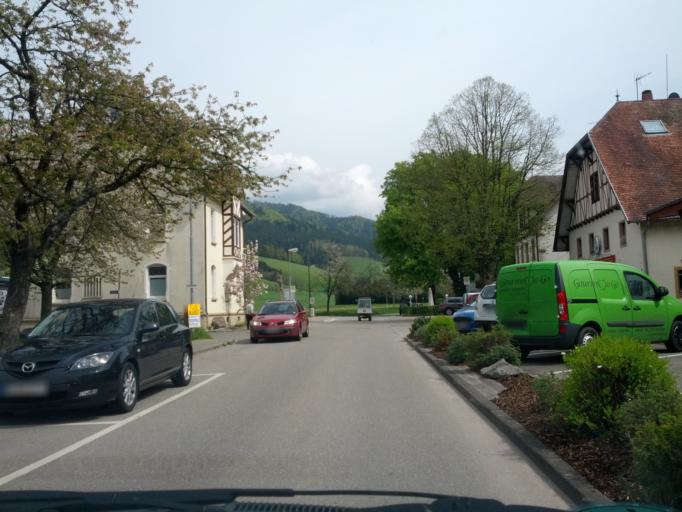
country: DE
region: Baden-Wuerttemberg
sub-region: Freiburg Region
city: Gutach im Breisgau
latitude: 48.1211
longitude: 8.0116
